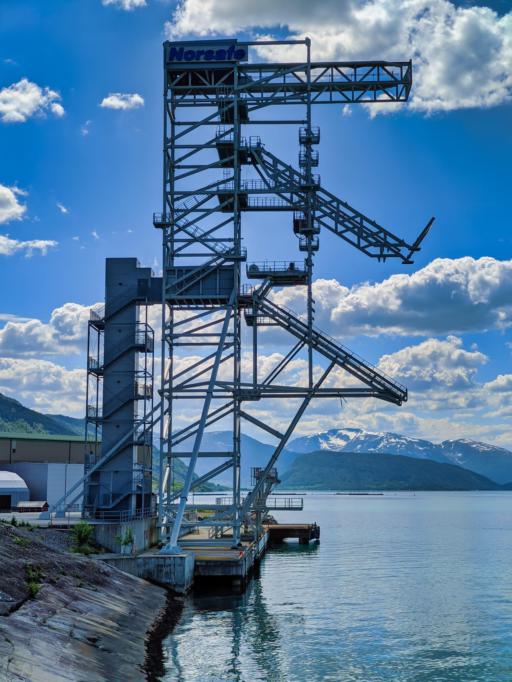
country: NO
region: Hordaland
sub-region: Kvinnherad
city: Rosendal
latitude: 60.0538
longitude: 6.0189
